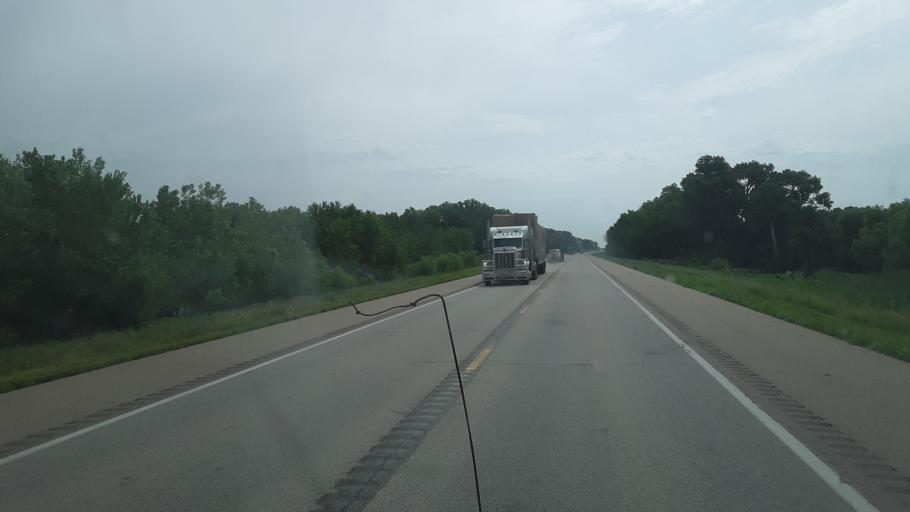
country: US
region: Kansas
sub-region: Stafford County
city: Stafford
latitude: 37.9845
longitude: -98.3756
